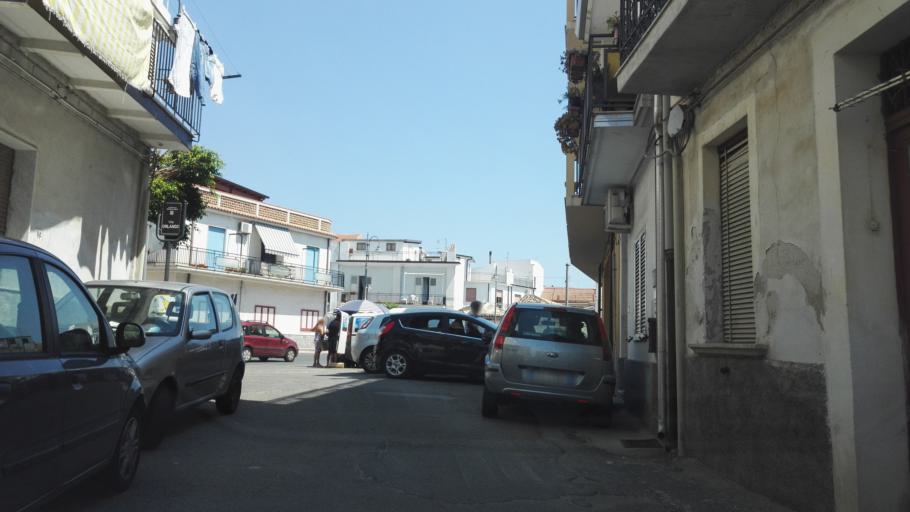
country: IT
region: Calabria
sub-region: Provincia di Reggio Calabria
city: Roccella Ionica
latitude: 38.3234
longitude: 16.4101
